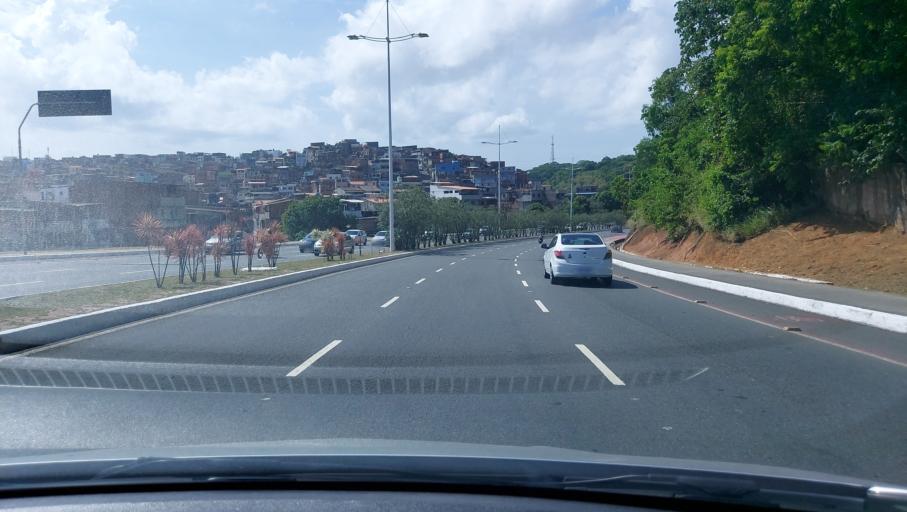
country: BR
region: Bahia
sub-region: Salvador
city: Salvador
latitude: -12.9717
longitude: -38.4520
